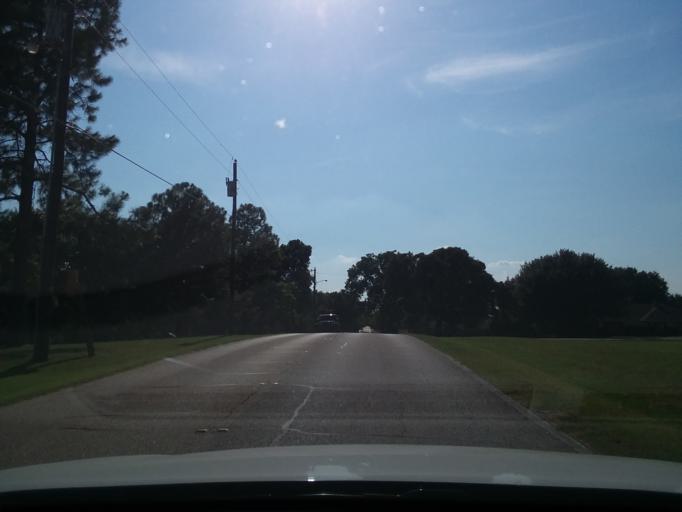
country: US
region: Texas
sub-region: Denton County
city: Double Oak
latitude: 33.0586
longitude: -97.1185
